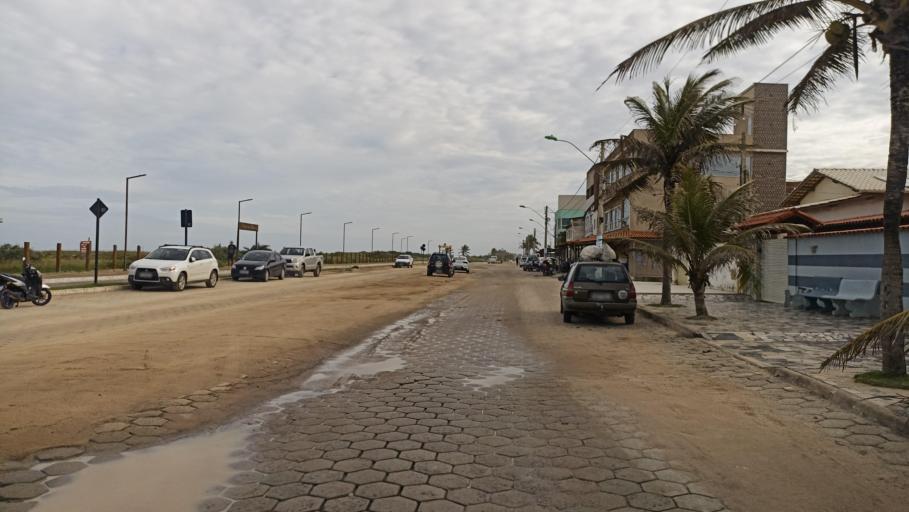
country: BR
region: Espirito Santo
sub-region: Sao Mateus
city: Sao Mateus
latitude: -18.7516
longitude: -39.7481
